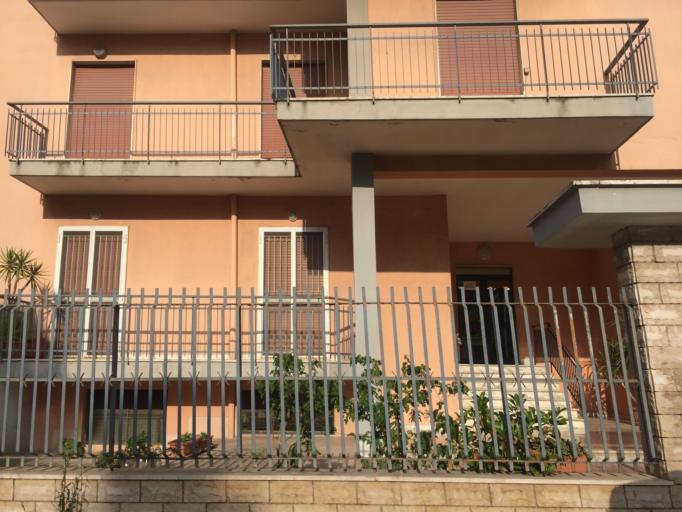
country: IT
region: Apulia
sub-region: Provincia di Bari
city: Capurso
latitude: 41.0455
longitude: 16.9187
